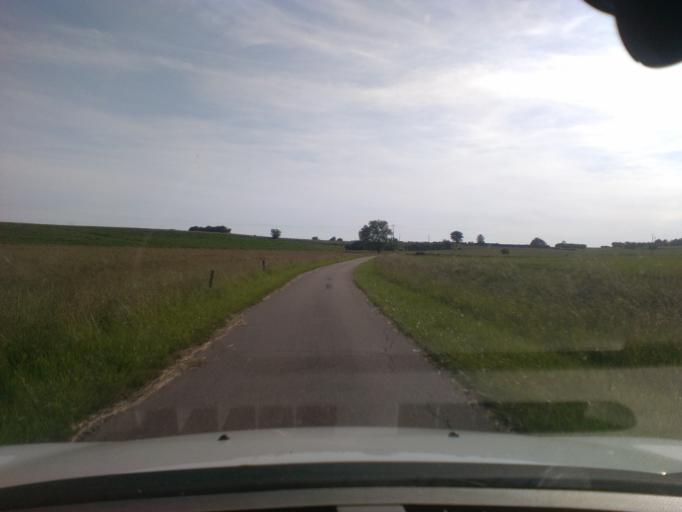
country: FR
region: Lorraine
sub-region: Departement des Vosges
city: Mirecourt
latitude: 48.2603
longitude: 6.2050
